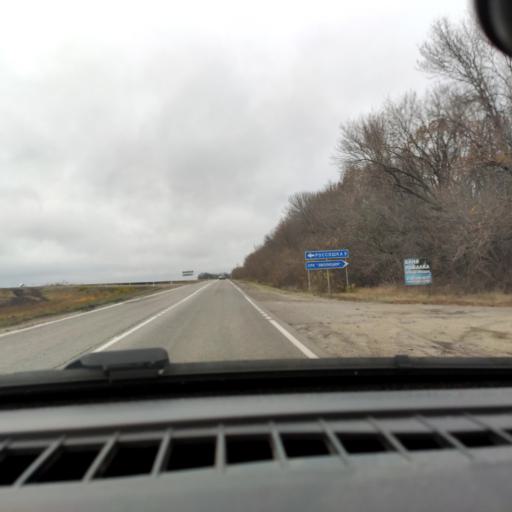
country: RU
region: Voronezj
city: Shilovo
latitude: 51.3842
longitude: 39.0092
